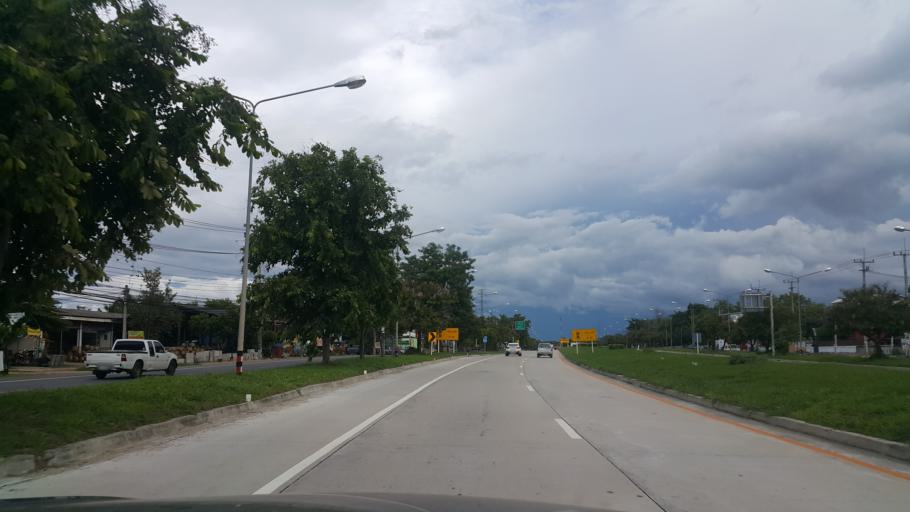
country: TH
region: Tak
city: Tak
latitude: 16.8998
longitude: 99.1275
